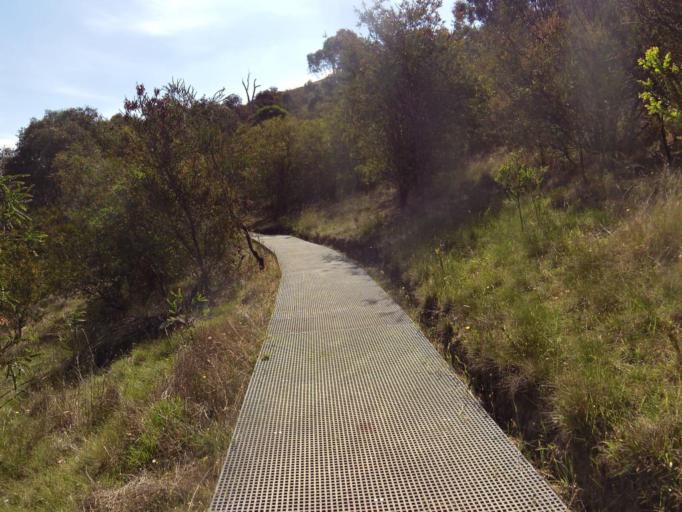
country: AU
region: Australian Capital Territory
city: Belconnen
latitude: -35.1573
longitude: 149.0796
